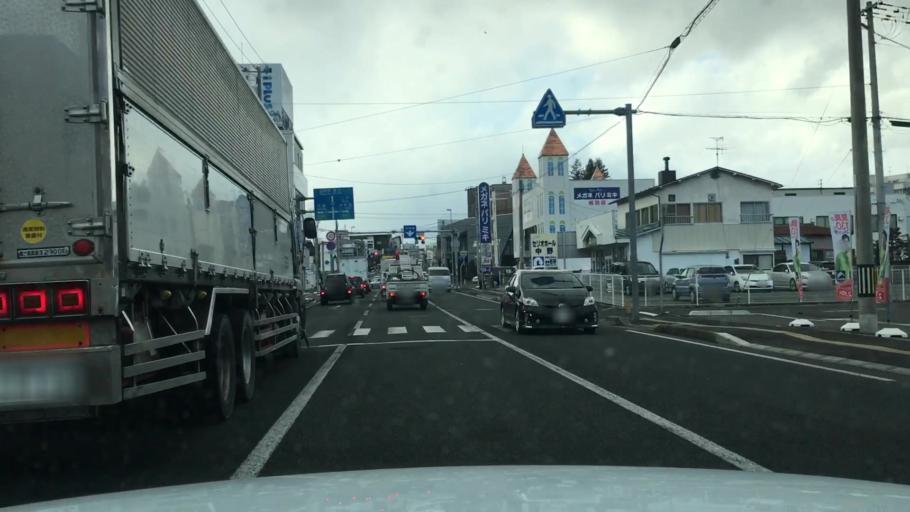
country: JP
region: Iwate
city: Morioka-shi
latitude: 39.6946
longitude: 141.1684
